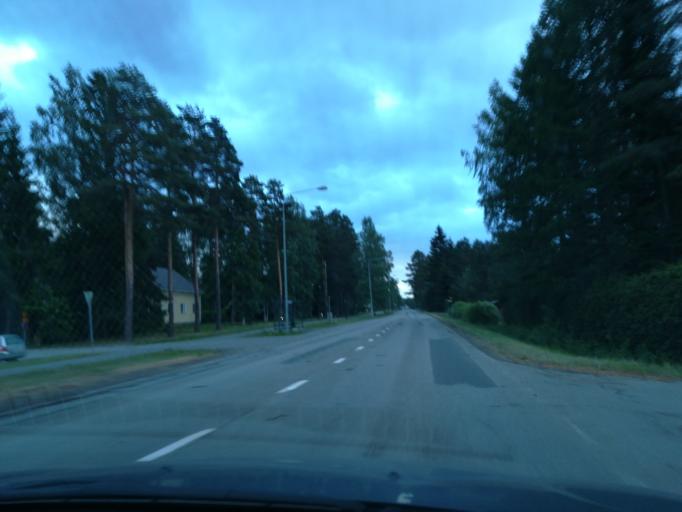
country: FI
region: Southern Savonia
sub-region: Mikkeli
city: Ristiina
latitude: 61.5101
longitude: 27.2487
